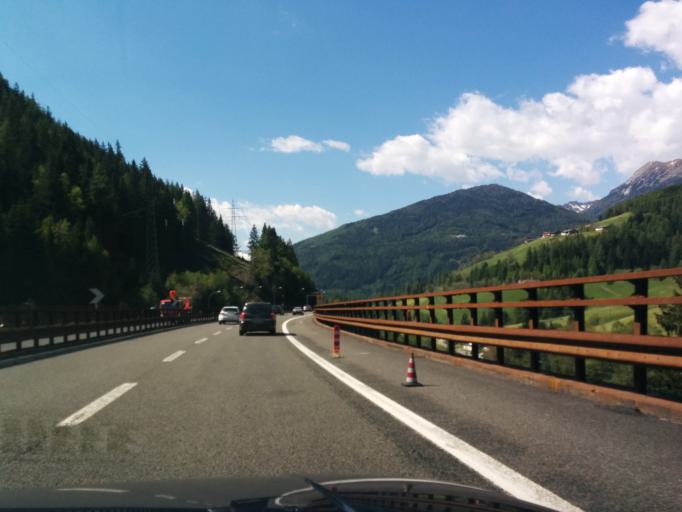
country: IT
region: Trentino-Alto Adige
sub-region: Bolzano
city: Colle Isarco
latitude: 46.9539
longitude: 11.4578
